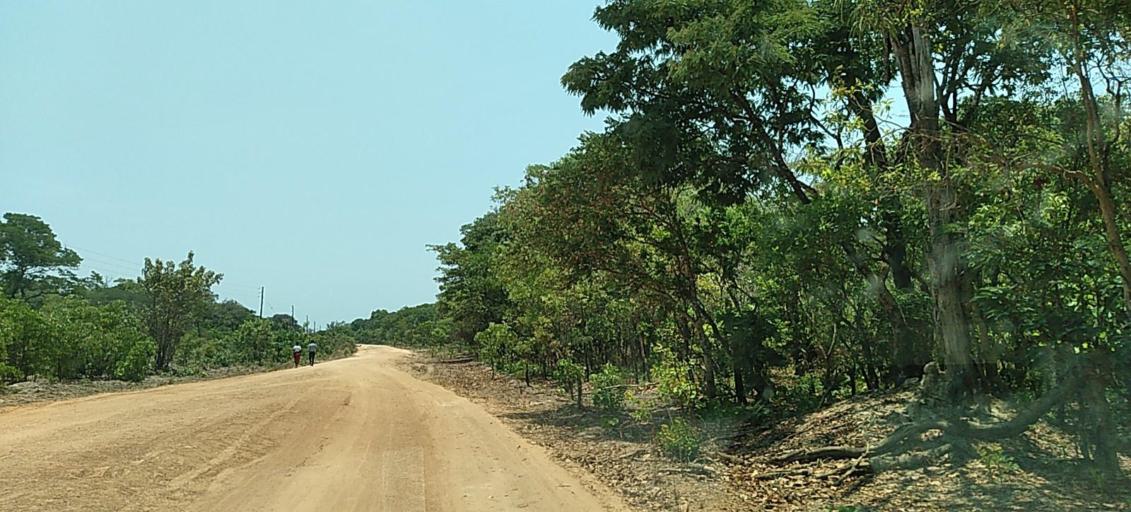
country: ZM
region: Copperbelt
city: Mpongwe
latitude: -13.8033
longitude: 27.8586
